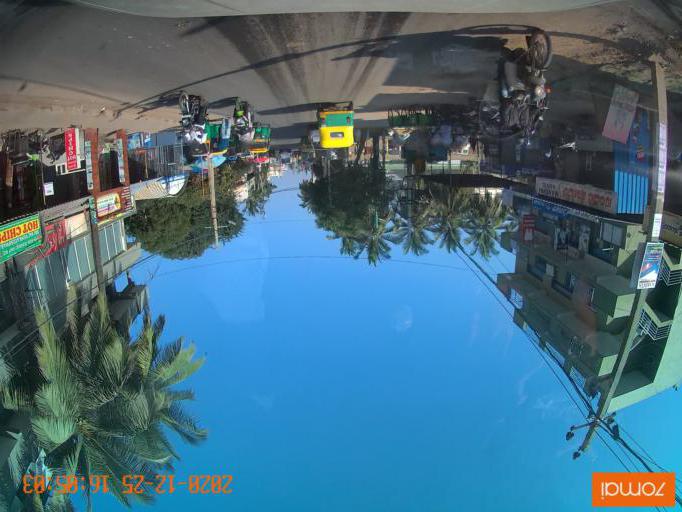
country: IN
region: Karnataka
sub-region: Bangalore Urban
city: Bangalore
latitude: 12.8881
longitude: 77.6256
